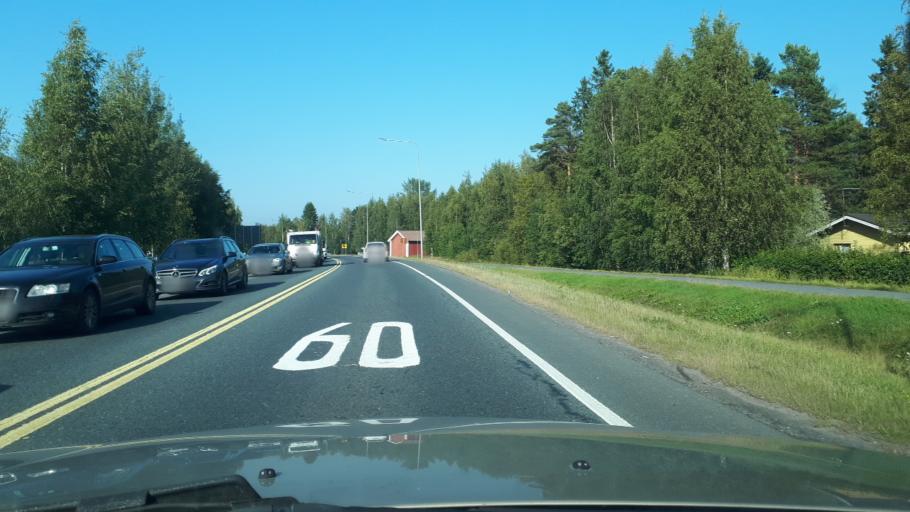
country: FI
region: Northern Ostrobothnia
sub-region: Oulunkaari
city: Ii
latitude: 65.3229
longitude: 25.3795
